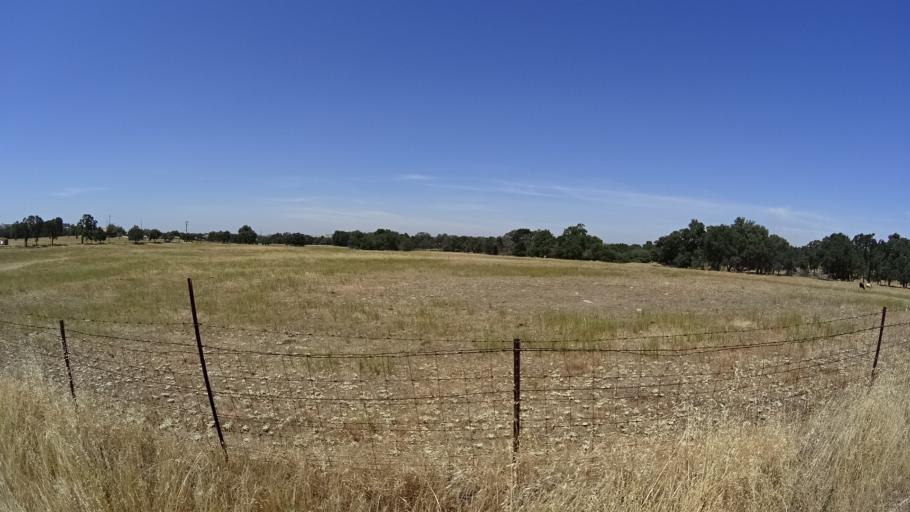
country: US
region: California
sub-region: Calaveras County
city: Rancho Calaveras
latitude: 38.1682
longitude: -120.9183
